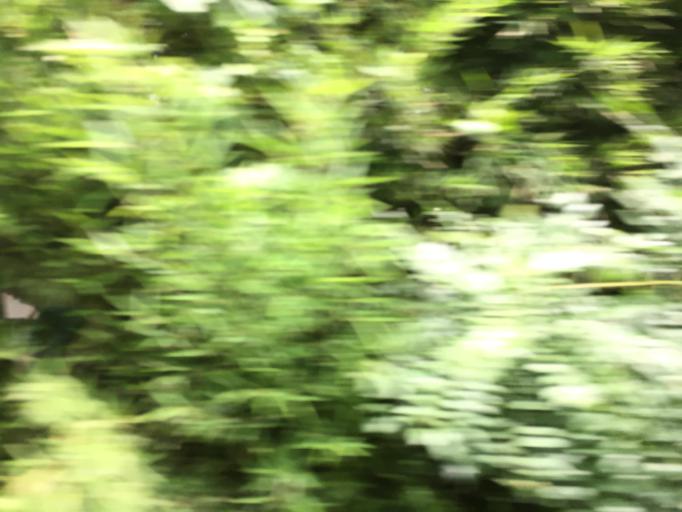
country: GT
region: Guatemala
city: Villa Canales
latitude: 14.4322
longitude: -90.5354
